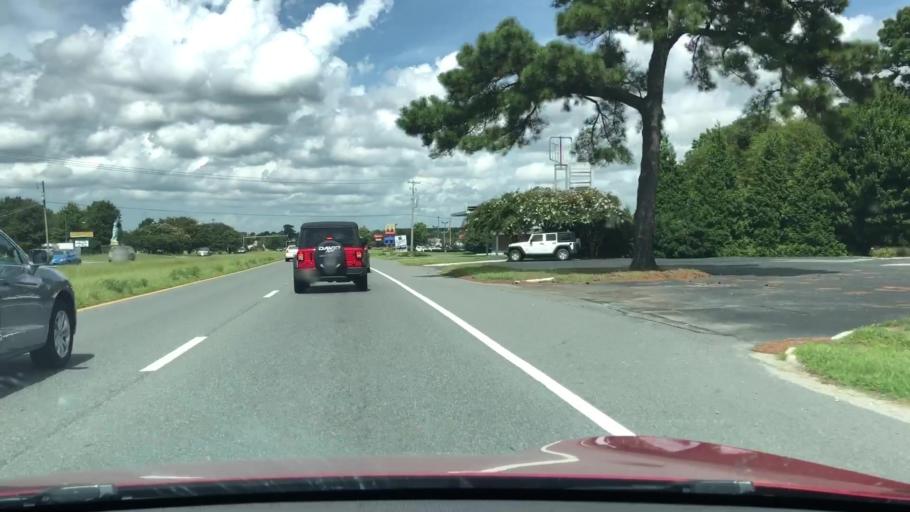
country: US
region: Virginia
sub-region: Northampton County
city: Exmore
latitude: 37.5184
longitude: -75.8318
